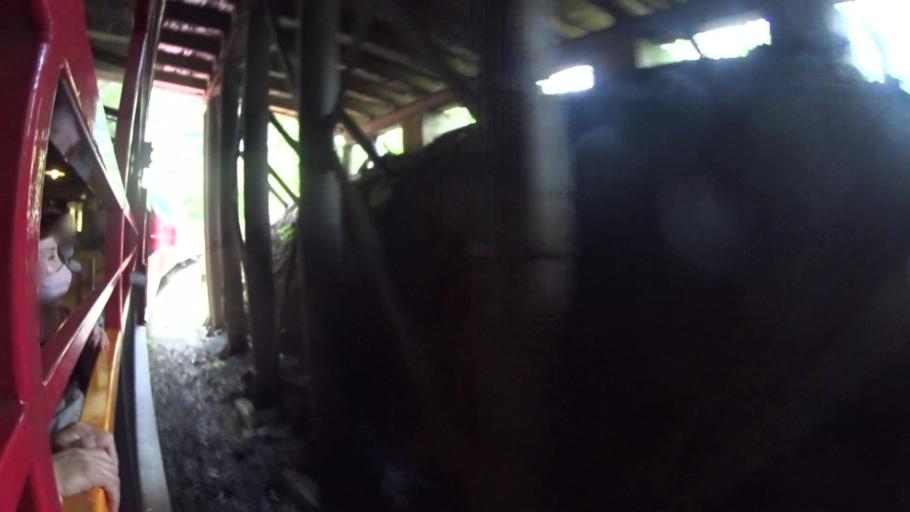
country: JP
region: Kyoto
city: Kameoka
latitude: 35.0173
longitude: 135.6249
